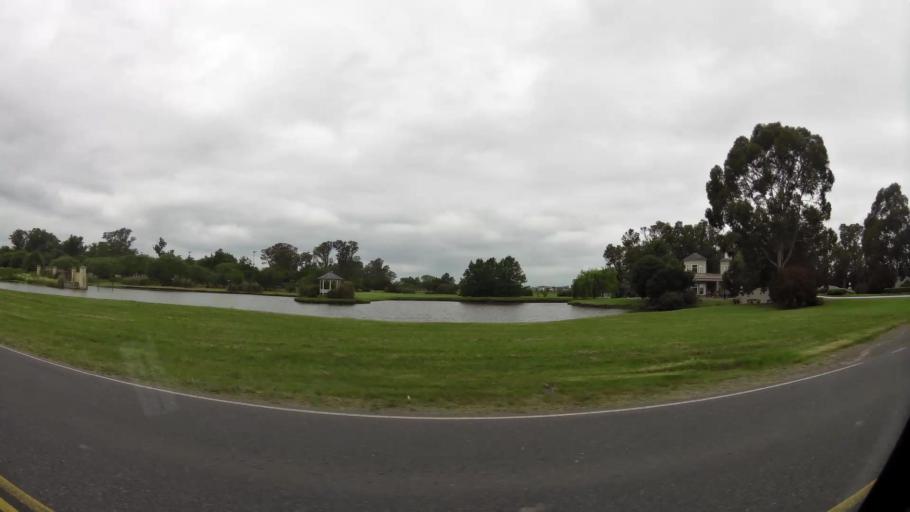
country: AR
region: Buenos Aires
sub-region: Partido de San Vicente
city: San Vicente
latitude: -34.9953
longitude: -58.4697
